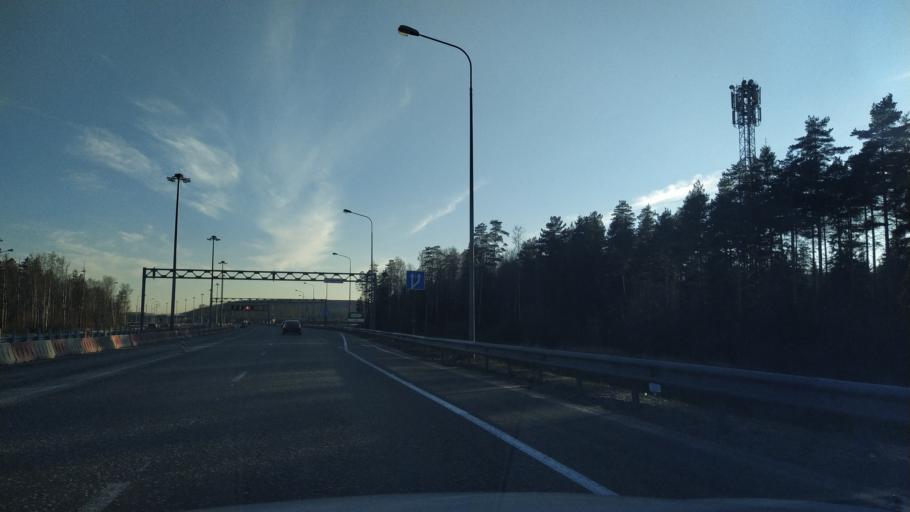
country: RU
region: St.-Petersburg
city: Levashovo
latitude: 60.0798
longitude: 30.1896
